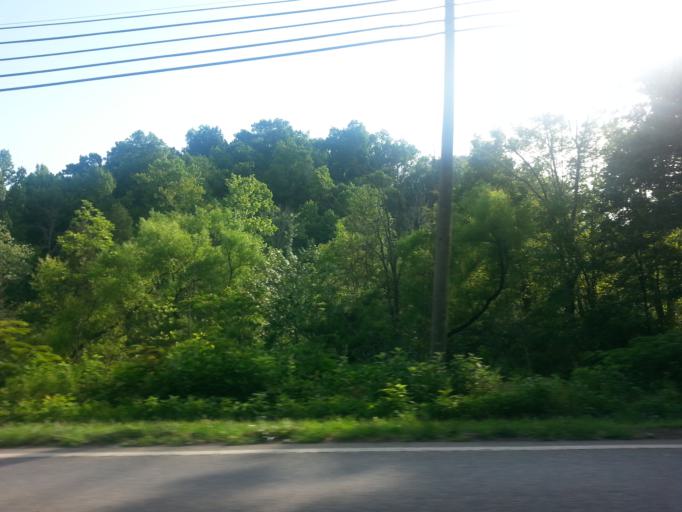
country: US
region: Tennessee
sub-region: Blount County
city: Louisville
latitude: 35.8046
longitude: -84.0224
